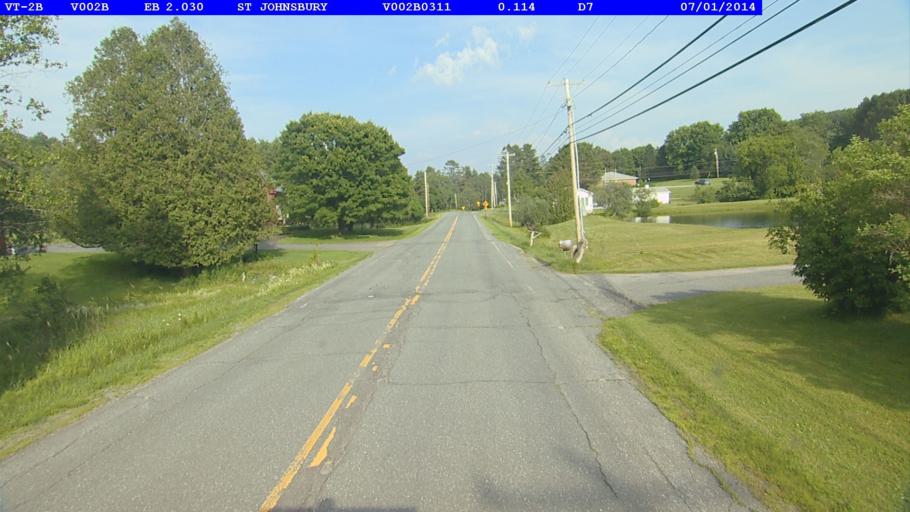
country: US
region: Vermont
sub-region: Caledonia County
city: St Johnsbury
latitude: 44.4288
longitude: -72.0538
